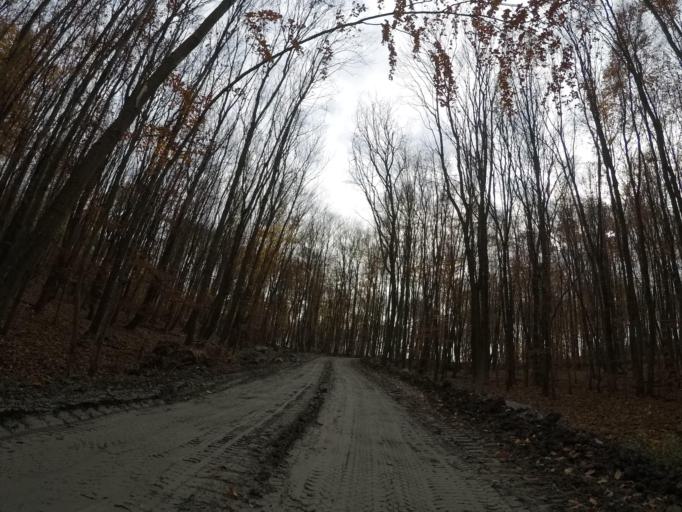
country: SK
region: Presovsky
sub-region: Okres Presov
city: Presov
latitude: 48.9731
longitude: 21.2167
